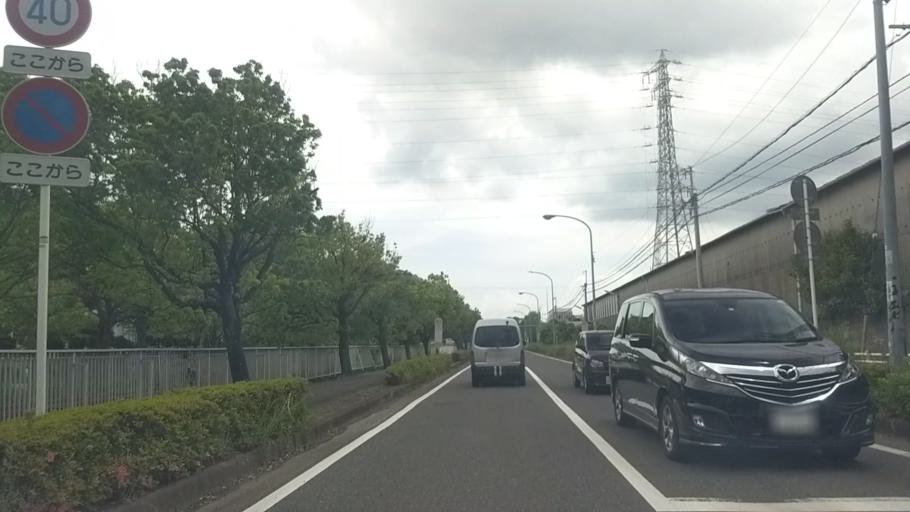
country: JP
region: Kanagawa
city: Fujisawa
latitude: 35.3718
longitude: 139.5226
